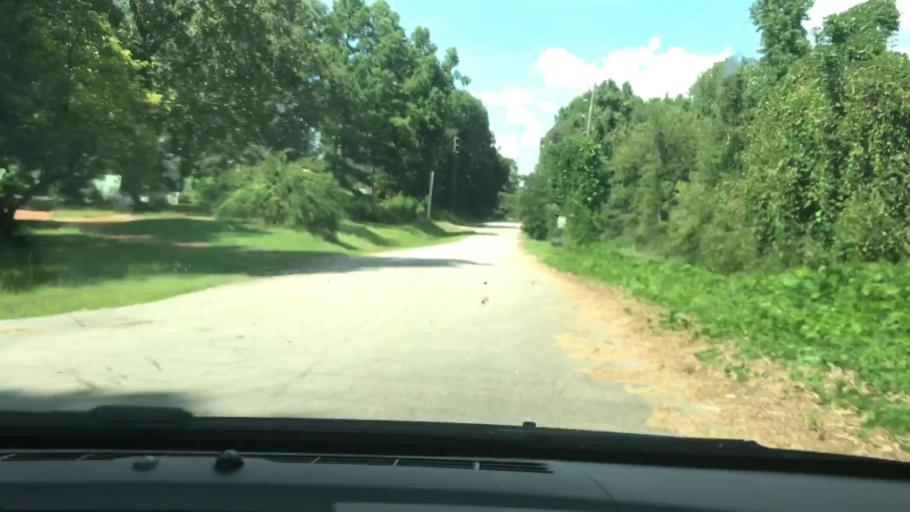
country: US
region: Georgia
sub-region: Troup County
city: La Grange
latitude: 33.0911
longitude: -85.1299
